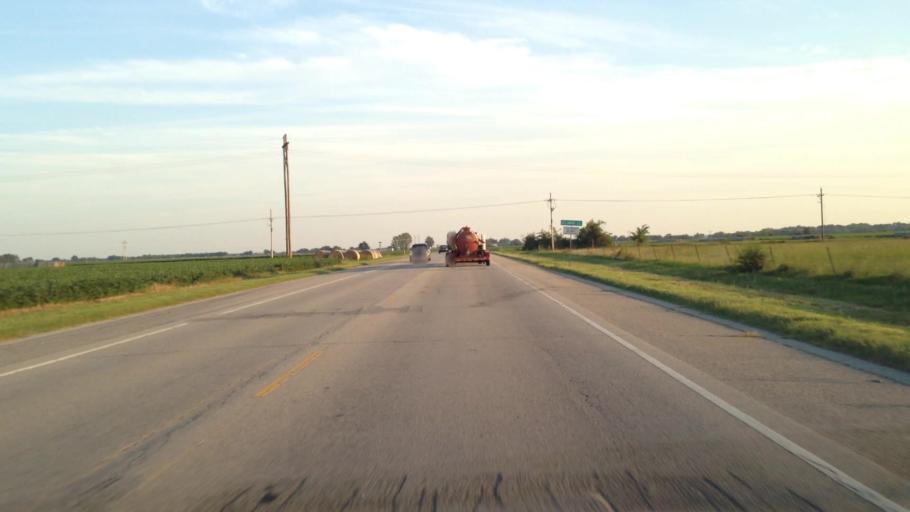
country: US
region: Oklahoma
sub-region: Ottawa County
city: Afton
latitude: 36.6724
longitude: -94.9814
